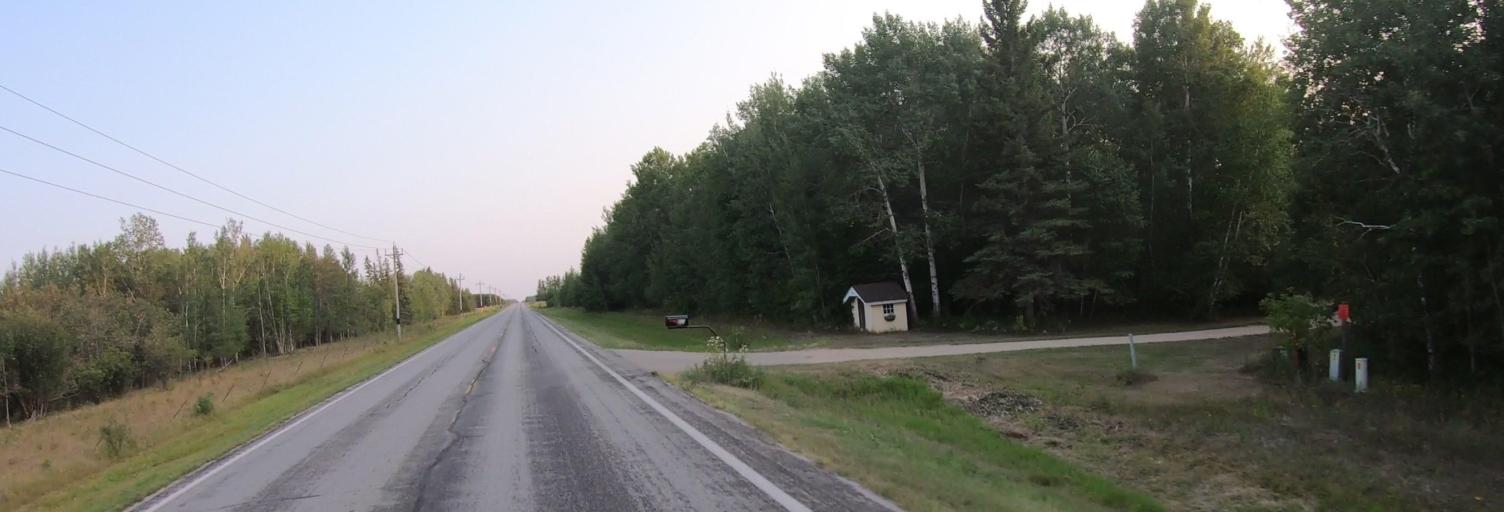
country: US
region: Minnesota
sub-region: Roseau County
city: Warroad
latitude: 48.8243
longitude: -95.3307
